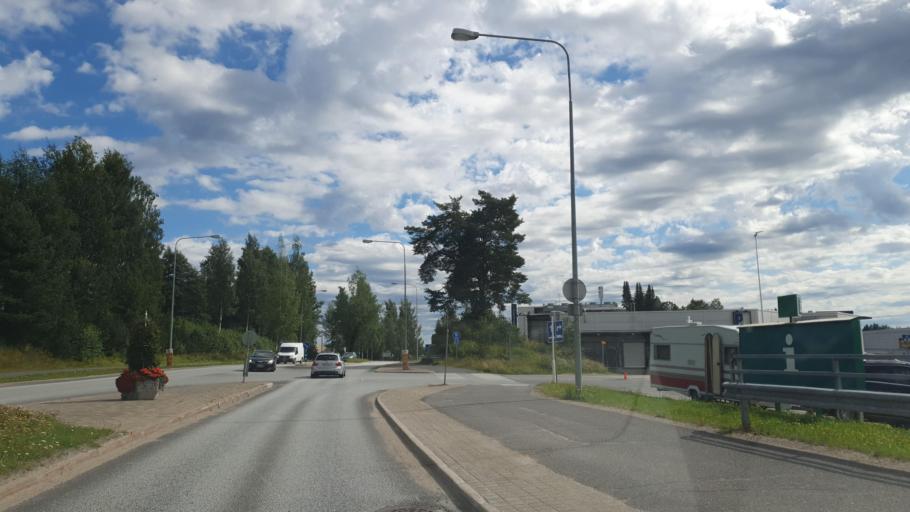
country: FI
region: Central Finland
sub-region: Jyvaeskylae
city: Muurame
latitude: 62.1381
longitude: 25.6725
